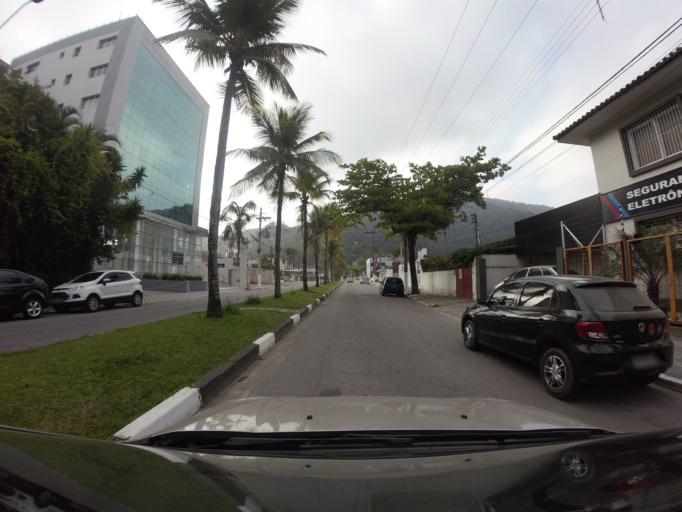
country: BR
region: Sao Paulo
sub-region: Guaruja
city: Guaruja
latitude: -23.9919
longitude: -46.2547
